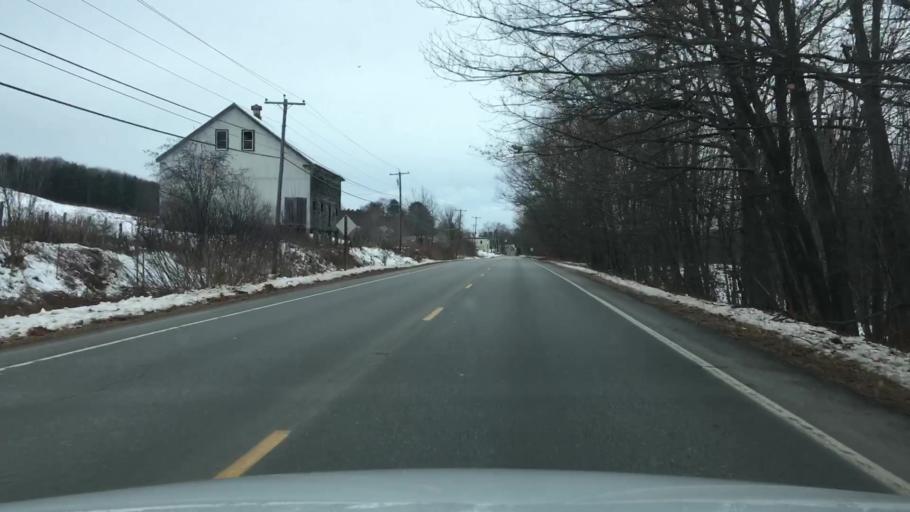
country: US
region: Maine
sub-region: Androscoggin County
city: Lewiston
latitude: 44.0669
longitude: -70.2090
